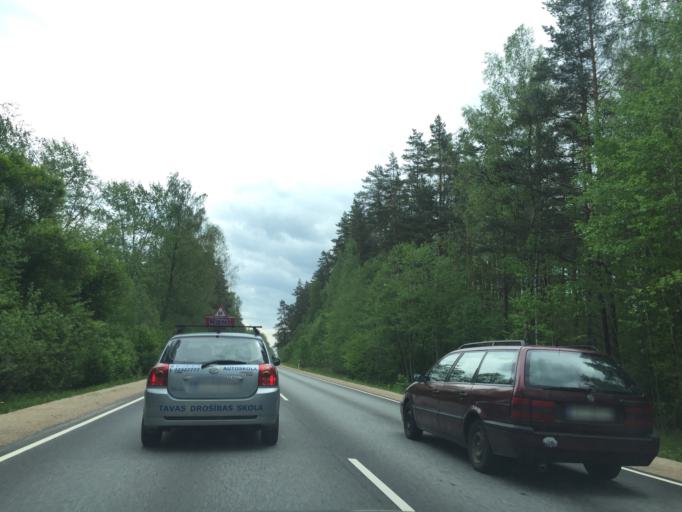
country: LV
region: Ikskile
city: Ikskile
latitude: 56.8900
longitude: 24.4792
